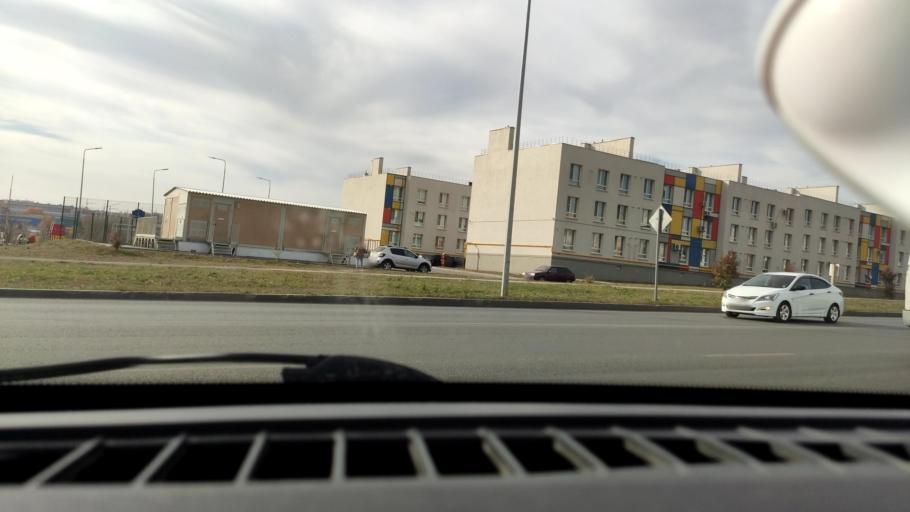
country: RU
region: Samara
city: Petra-Dubrava
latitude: 53.3123
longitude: 50.3079
